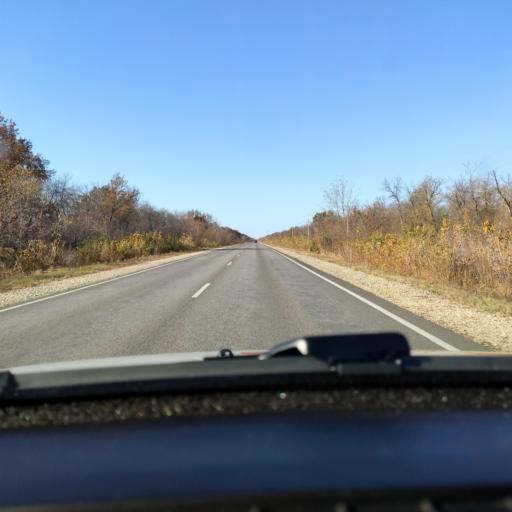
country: RU
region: Voronezj
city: Latnaya
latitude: 51.8075
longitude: 38.8603
